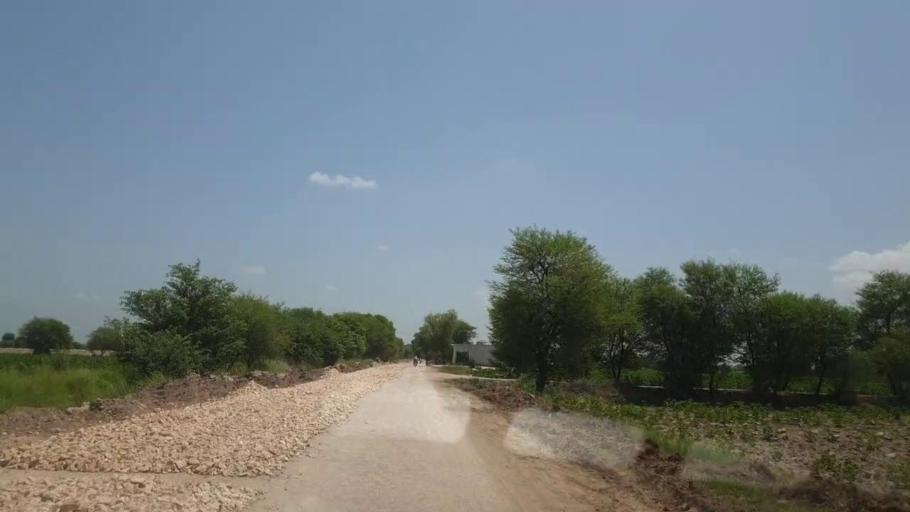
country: PK
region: Sindh
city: Pano Aqil
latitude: 27.6660
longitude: 69.1873
